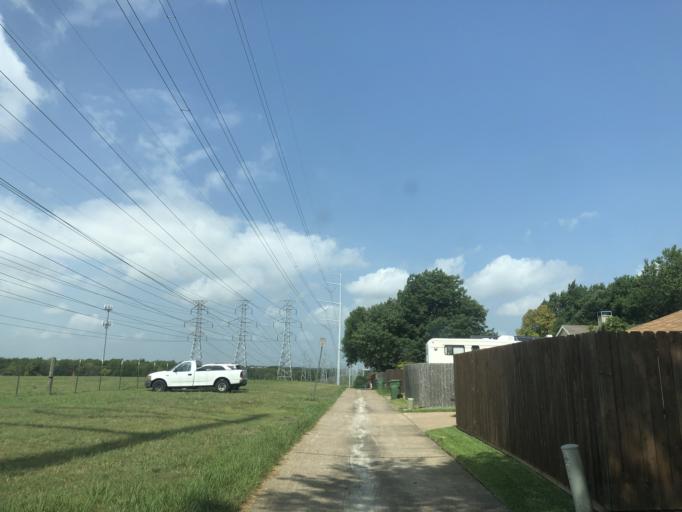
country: US
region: Texas
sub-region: Dallas County
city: Sunnyvale
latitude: 32.8344
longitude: -96.5629
